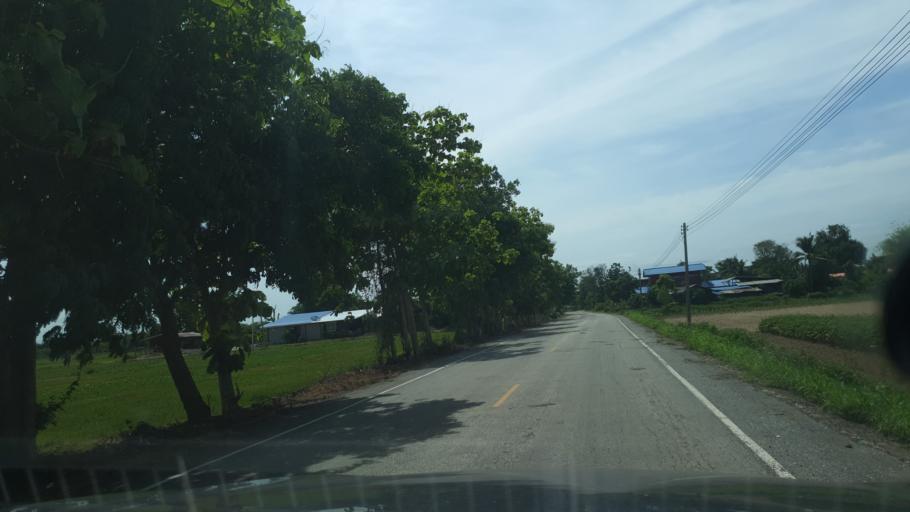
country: TH
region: Sukhothai
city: Si Samrong
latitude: 17.1968
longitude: 99.7273
